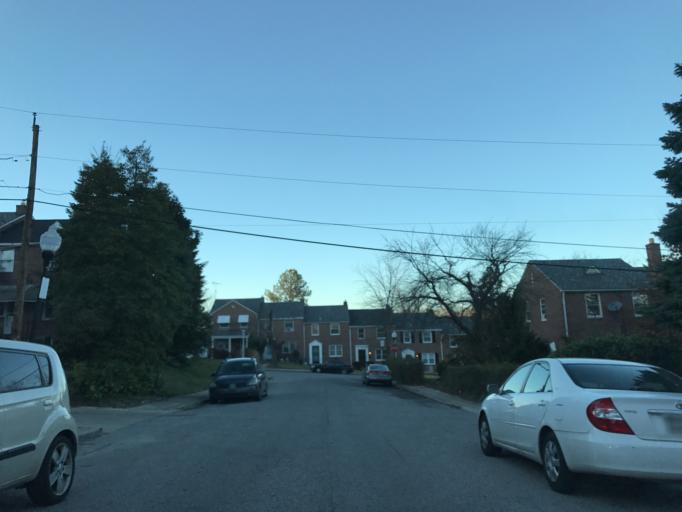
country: US
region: Maryland
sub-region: City of Baltimore
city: Baltimore
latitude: 39.3362
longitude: -76.6002
